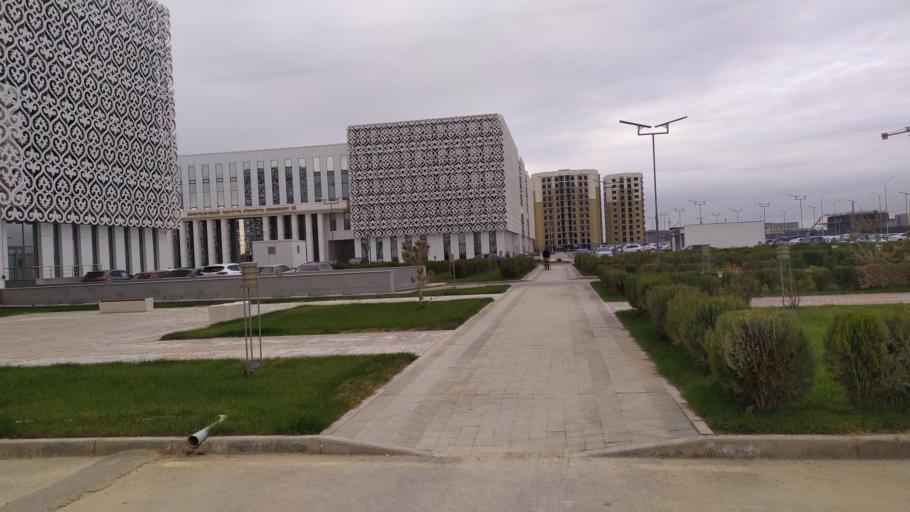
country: KZ
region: Ongtustik Qazaqstan
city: Turkestan
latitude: 43.2779
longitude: 68.3501
